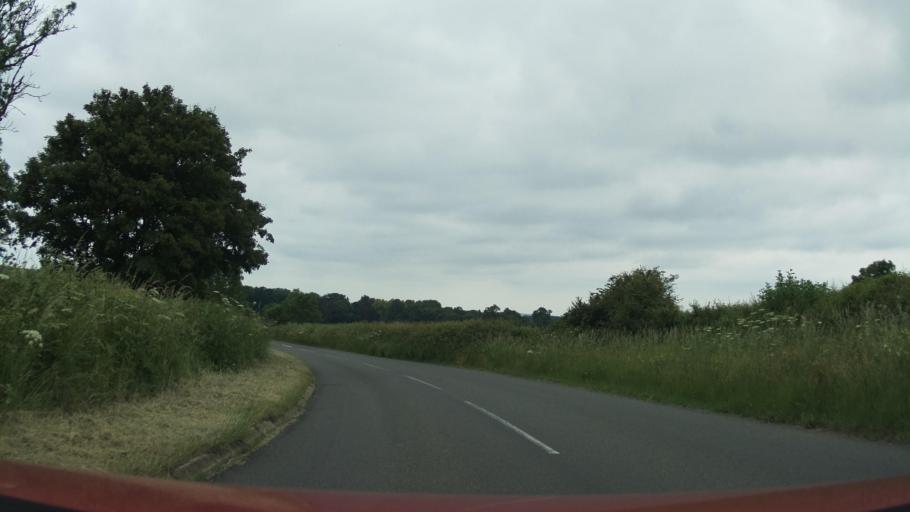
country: GB
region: England
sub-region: Leicestershire
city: Melton Mowbray
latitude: 52.7065
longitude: -0.8339
